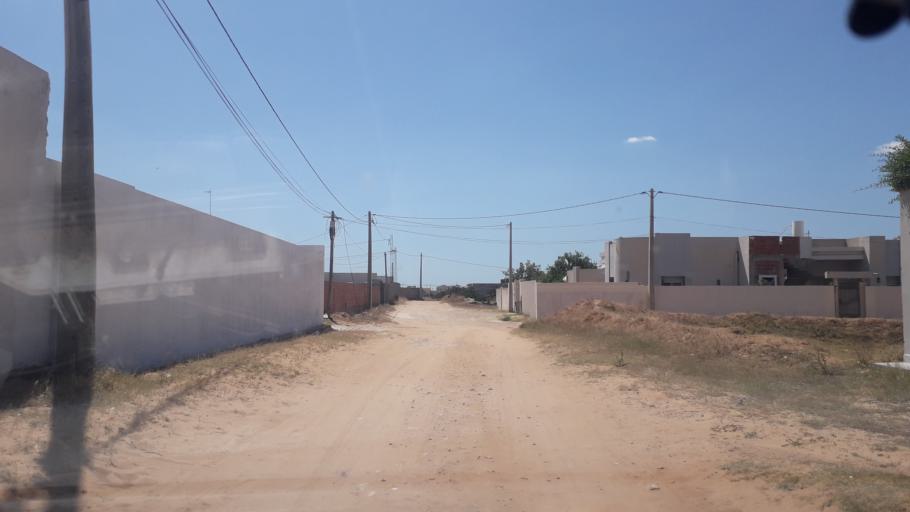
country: TN
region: Safaqis
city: Al Qarmadah
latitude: 34.8319
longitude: 10.7707
